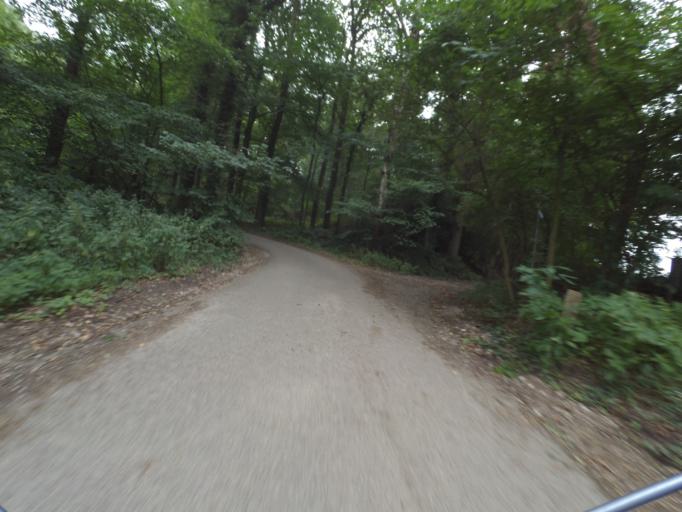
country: NL
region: Overijssel
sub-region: Gemeente Oldenzaal
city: Oldenzaal
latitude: 52.3239
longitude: 6.9535
